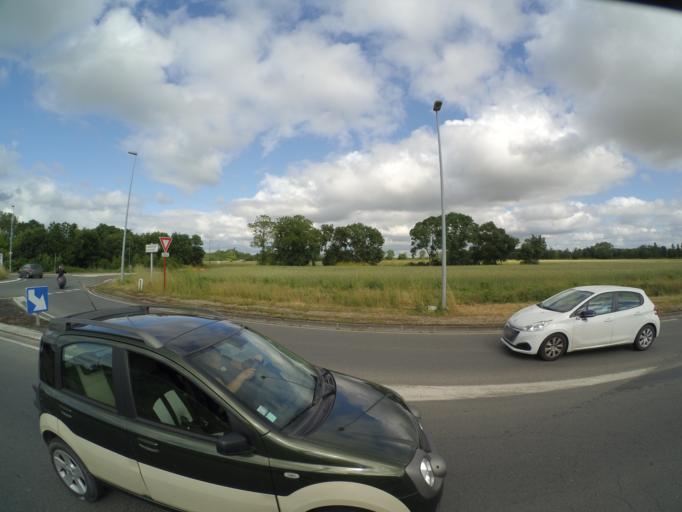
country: FR
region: Aquitaine
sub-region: Departement de la Gironde
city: Saint-Louis-de-Montferrand
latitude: 44.9435
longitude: -0.5603
